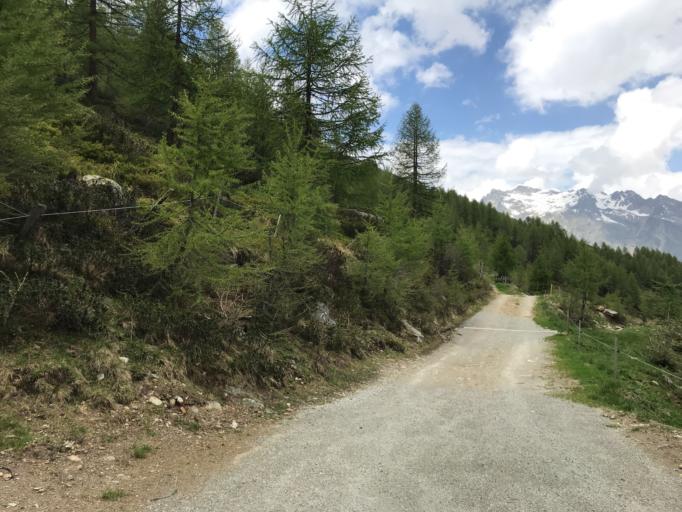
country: CH
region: Grisons
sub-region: Maloja District
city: Silvaplana
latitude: 46.3863
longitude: 9.7817
